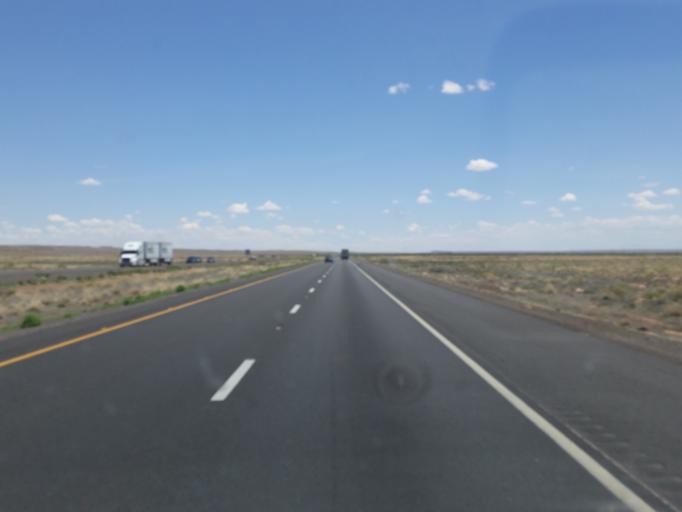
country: US
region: Arizona
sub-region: Navajo County
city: Winslow
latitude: 34.9998
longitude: -110.5982
